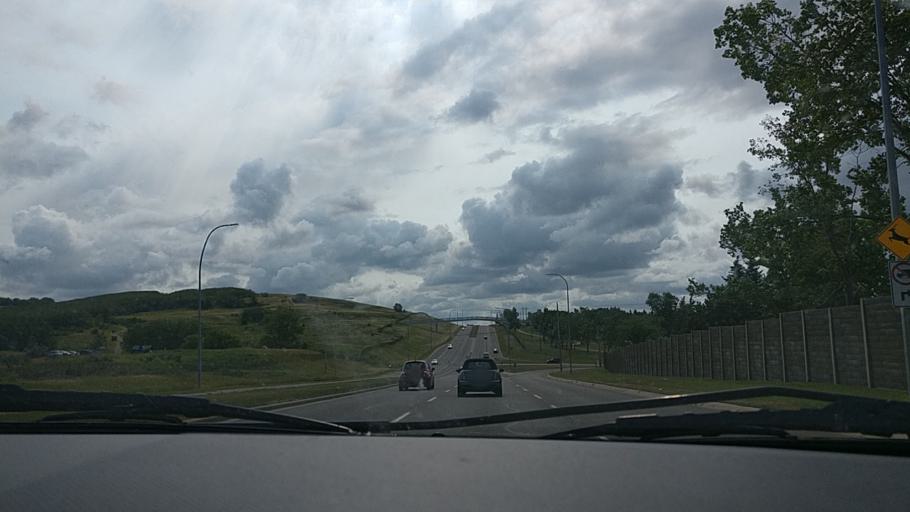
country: CA
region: Alberta
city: Calgary
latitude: 51.1043
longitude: -114.1296
